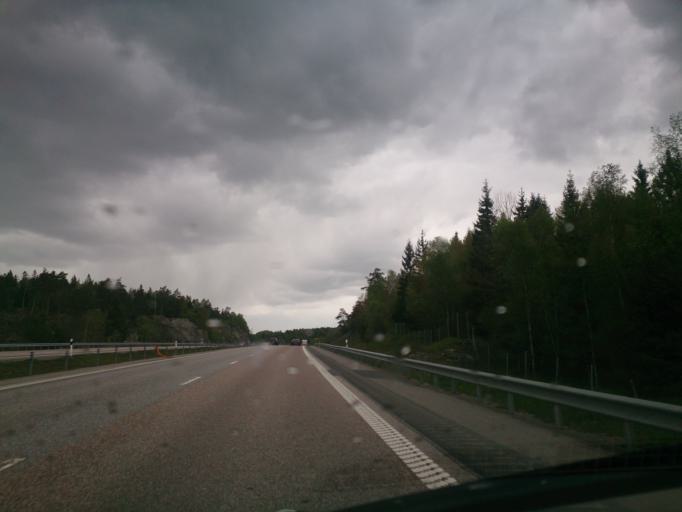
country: SE
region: Soedermanland
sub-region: Trosa Kommun
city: Vagnharad
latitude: 58.9877
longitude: 17.5331
